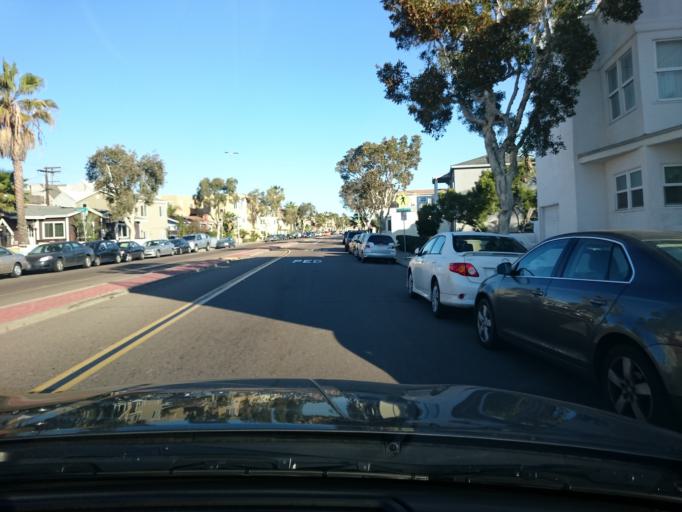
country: US
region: California
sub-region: San Diego County
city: La Jolla
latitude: 32.7755
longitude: -117.2521
